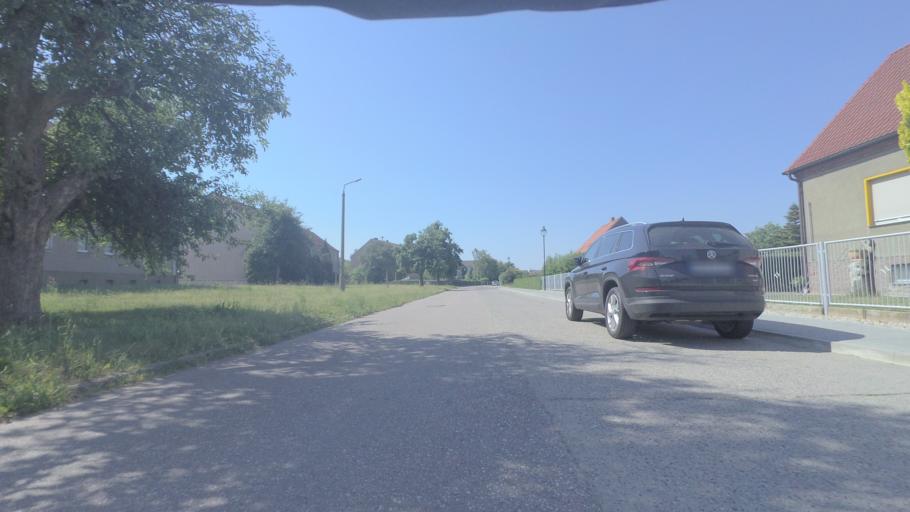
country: DE
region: Saxony-Anhalt
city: Vockerode
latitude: 51.8464
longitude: 12.3479
